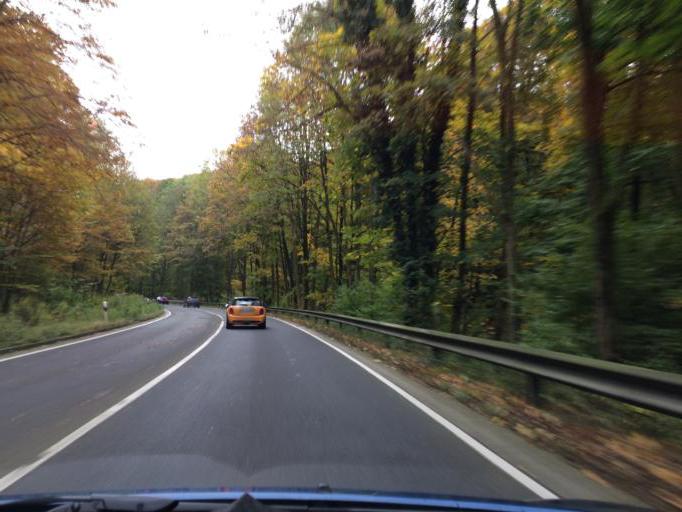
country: DE
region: North Rhine-Westphalia
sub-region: Regierungsbezirk Koln
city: Bad Honnef
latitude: 50.6768
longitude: 7.2329
